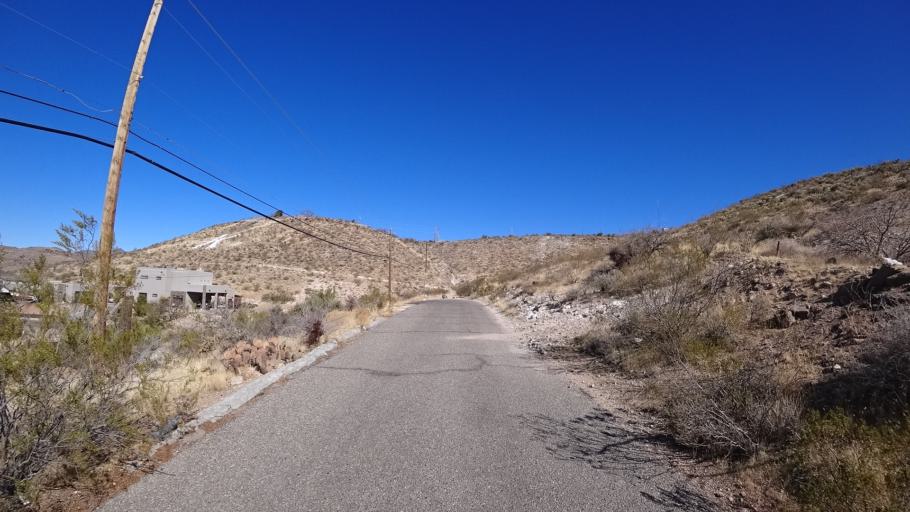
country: US
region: Arizona
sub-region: Mohave County
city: Kingman
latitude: 35.1946
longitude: -114.0539
